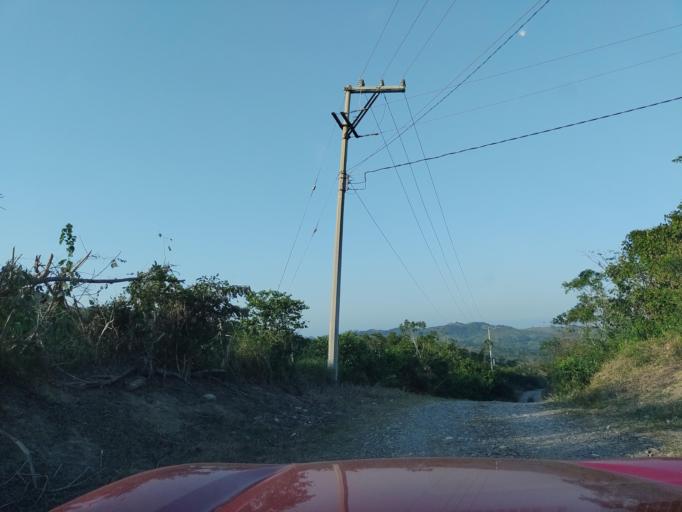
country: MX
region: Veracruz
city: Agua Dulce
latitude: 20.2875
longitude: -97.2469
